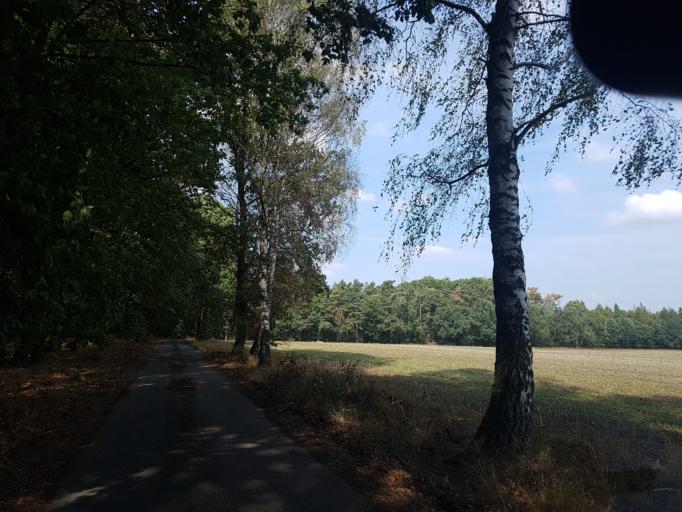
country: DE
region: Brandenburg
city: Gorzke
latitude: 52.0585
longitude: 12.2763
